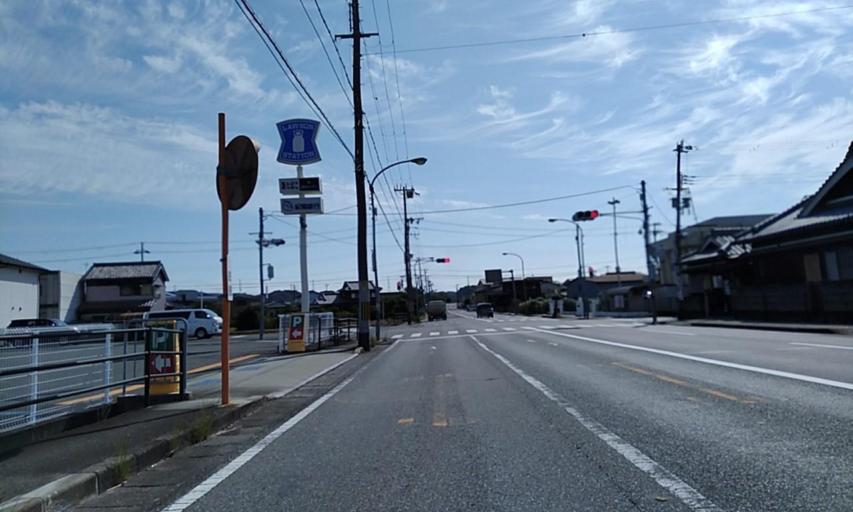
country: JP
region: Wakayama
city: Gobo
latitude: 33.8918
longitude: 135.1622
